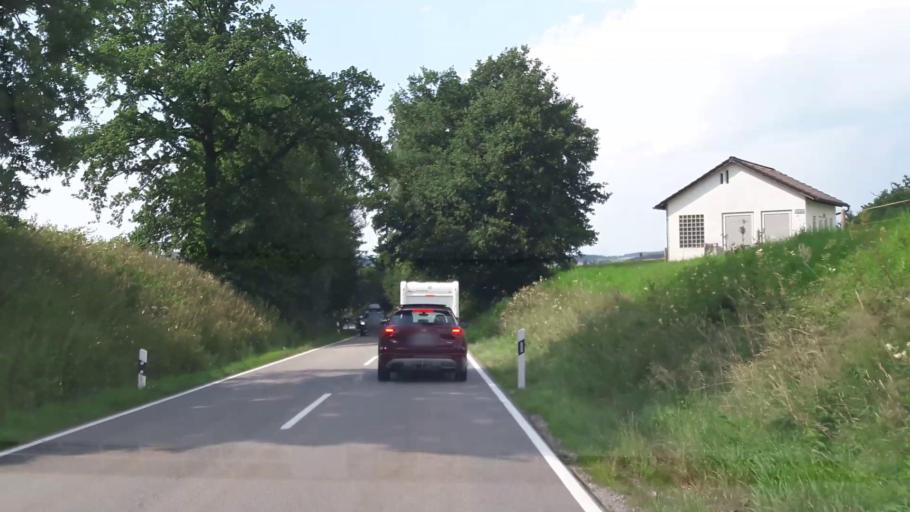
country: DE
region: Bavaria
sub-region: Upper Bavaria
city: Teisendorf
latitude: 47.8342
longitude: 12.8346
